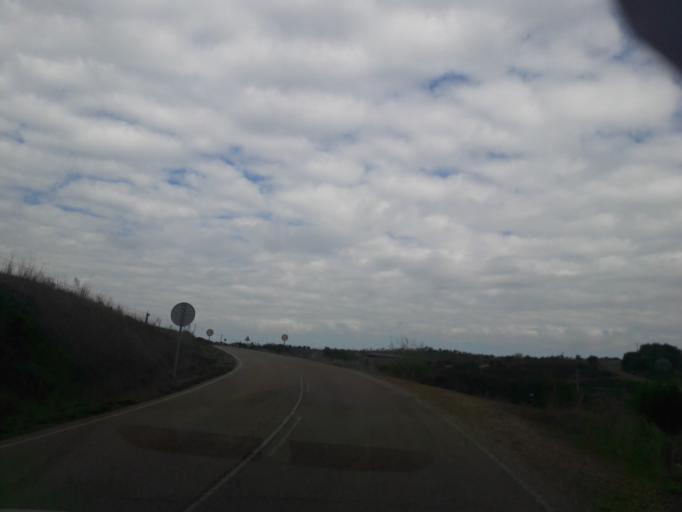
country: ES
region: Castille and Leon
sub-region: Provincia de Salamanca
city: Serradilla del Llano
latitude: 40.5033
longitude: -6.3600
